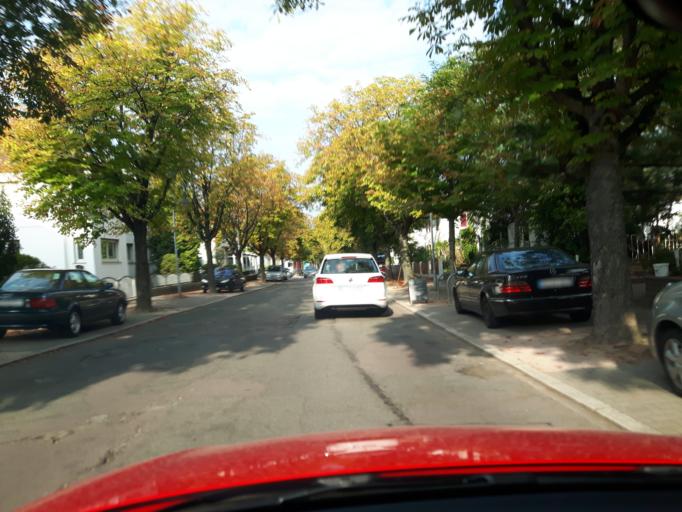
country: DE
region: Baden-Wuerttemberg
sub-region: Karlsruhe Region
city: Rheinstetten
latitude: 48.9745
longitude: 8.3160
